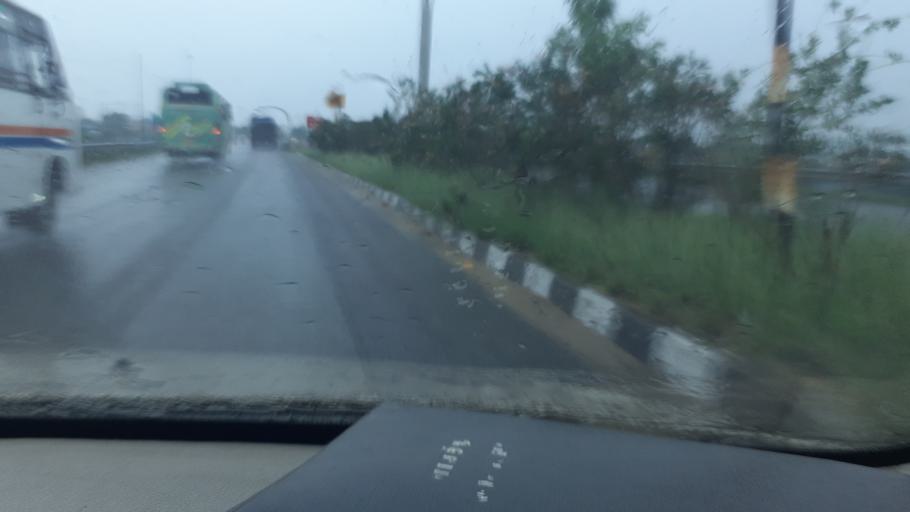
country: IN
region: Tamil Nadu
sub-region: Virudhunagar
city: Sattur
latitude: 9.3769
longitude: 77.9124
